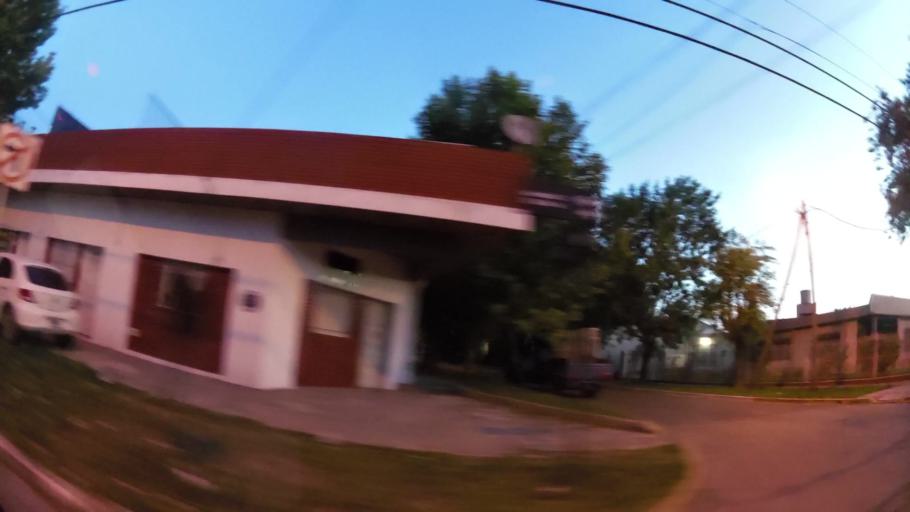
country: AR
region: Buenos Aires
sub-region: Partido de Quilmes
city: Quilmes
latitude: -34.7661
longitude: -58.1996
